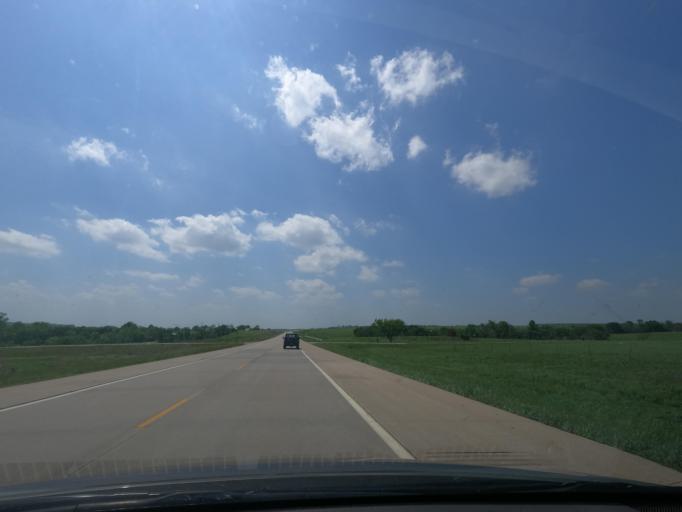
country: US
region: Kansas
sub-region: Elk County
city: Howard
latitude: 37.6280
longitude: -96.1239
